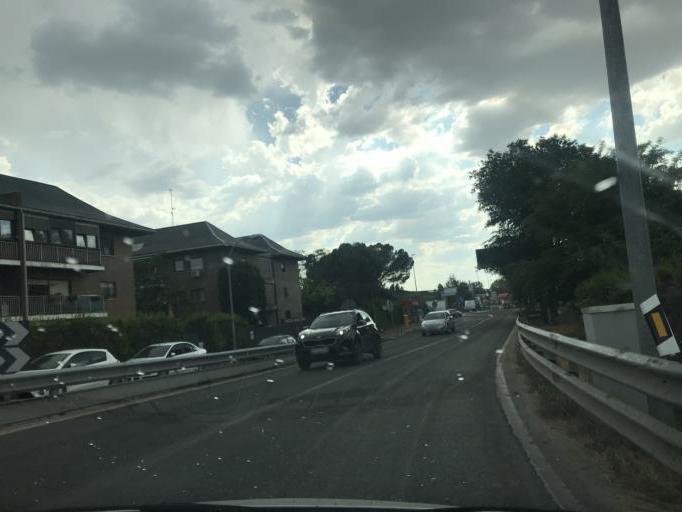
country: ES
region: Madrid
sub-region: Provincia de Madrid
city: Paracuellos de Jarama
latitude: 40.4998
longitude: -3.5449
